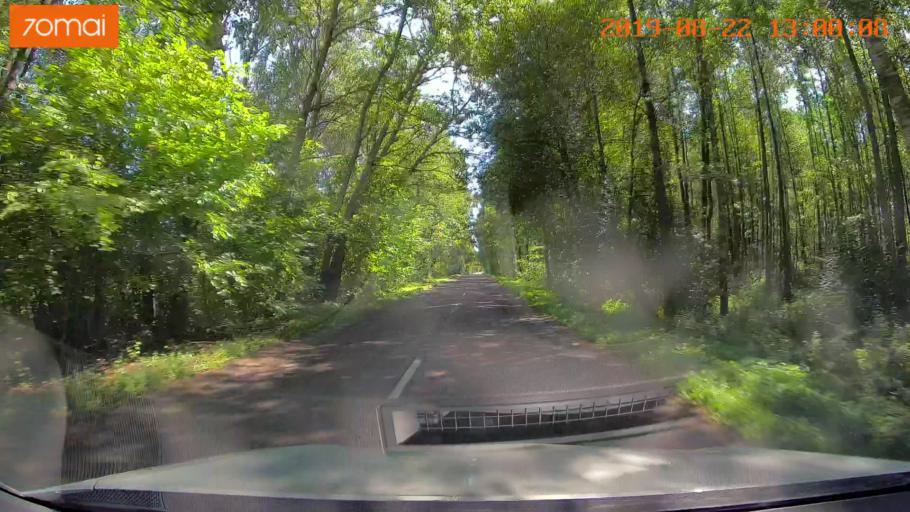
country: BY
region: Minsk
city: Prawdzinski
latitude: 53.4185
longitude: 27.8046
